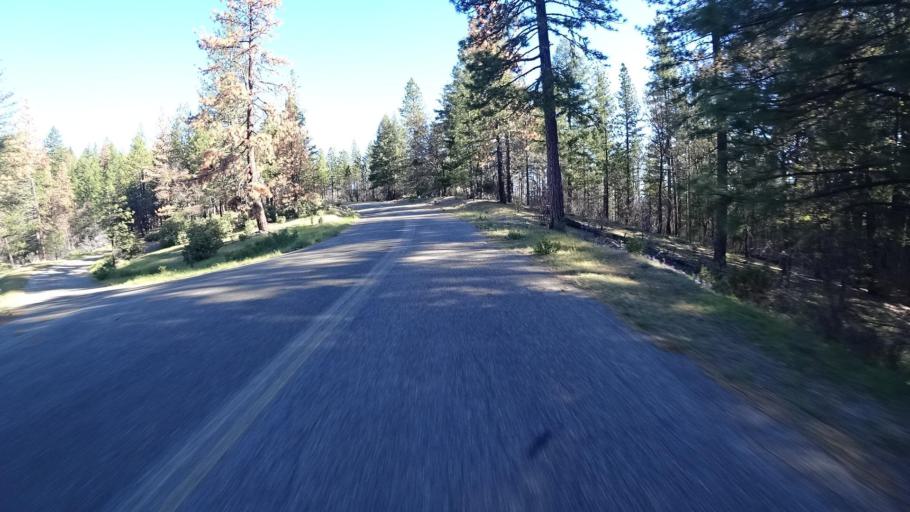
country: US
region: California
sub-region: Lake County
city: Upper Lake
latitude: 39.3063
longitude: -122.9359
